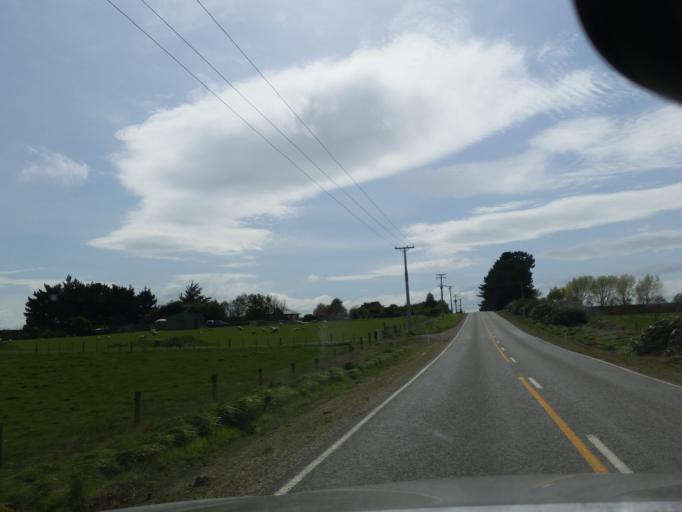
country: NZ
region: Southland
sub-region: Invercargill City
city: Invercargill
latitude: -46.3653
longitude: 168.4535
